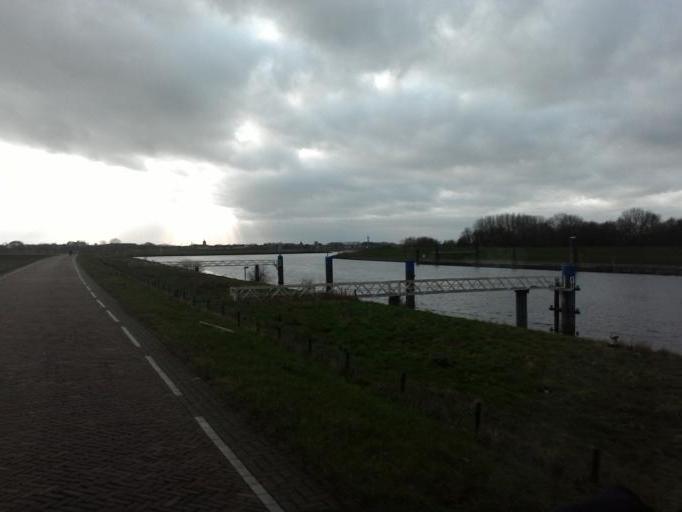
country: NL
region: Utrecht
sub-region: Gemeente Vianen
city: Vianen
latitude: 52.0081
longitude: 5.1080
